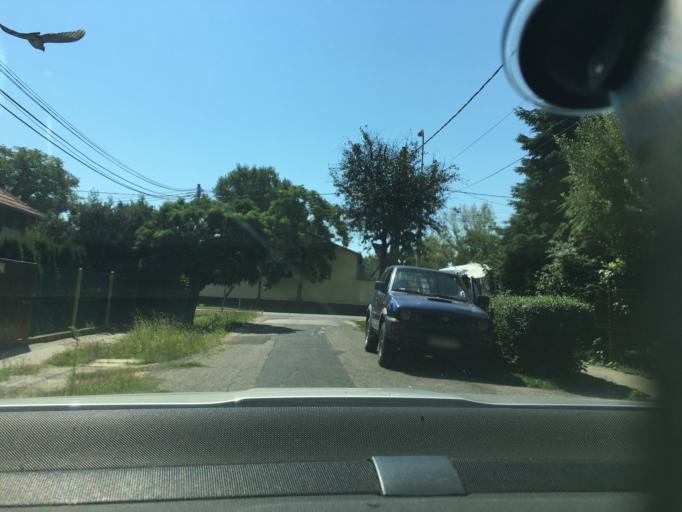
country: HU
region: Budapest
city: Budapest XVI. keruelet
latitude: 47.5050
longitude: 19.1917
